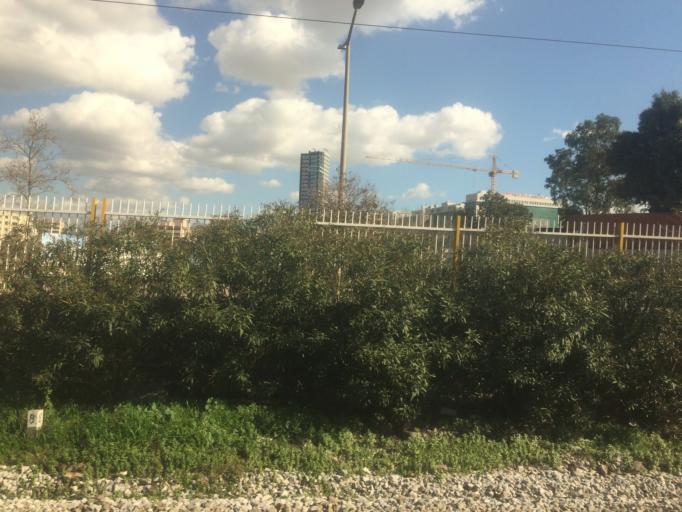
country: TR
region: Izmir
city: Buca
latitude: 38.4444
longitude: 27.1736
